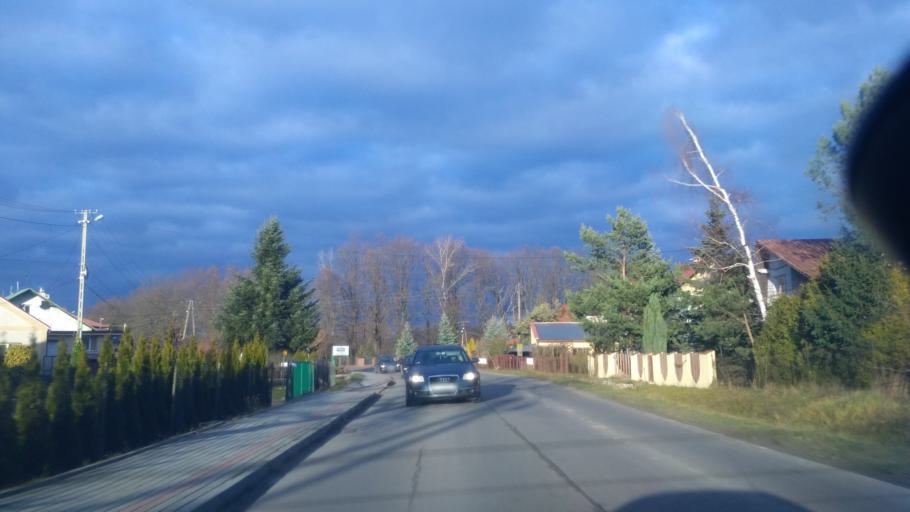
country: PL
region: Subcarpathian Voivodeship
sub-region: Powiat rzeszowski
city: Krasne
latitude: 50.0464
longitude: 22.1228
